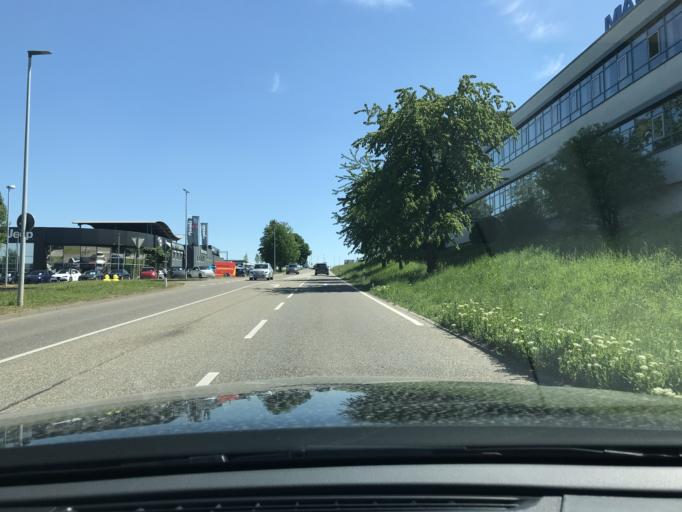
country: DE
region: Baden-Wuerttemberg
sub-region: Regierungsbezirk Stuttgart
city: Weinstadt-Endersbach
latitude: 48.8138
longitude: 9.3540
